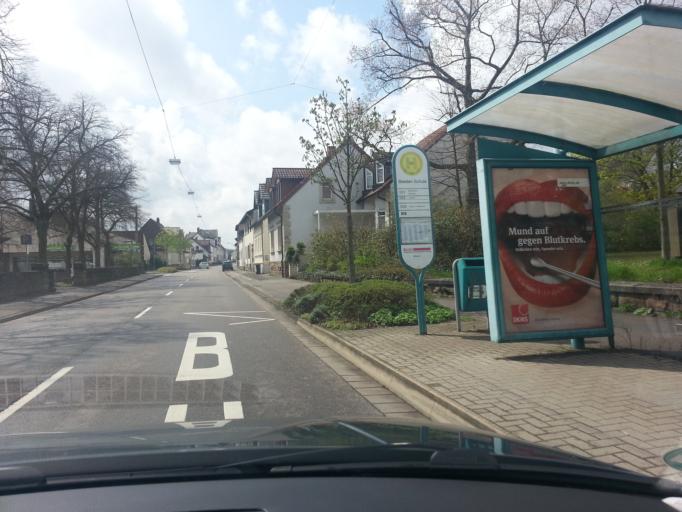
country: DE
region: Saarland
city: Homburg
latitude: 49.3104
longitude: 7.3173
